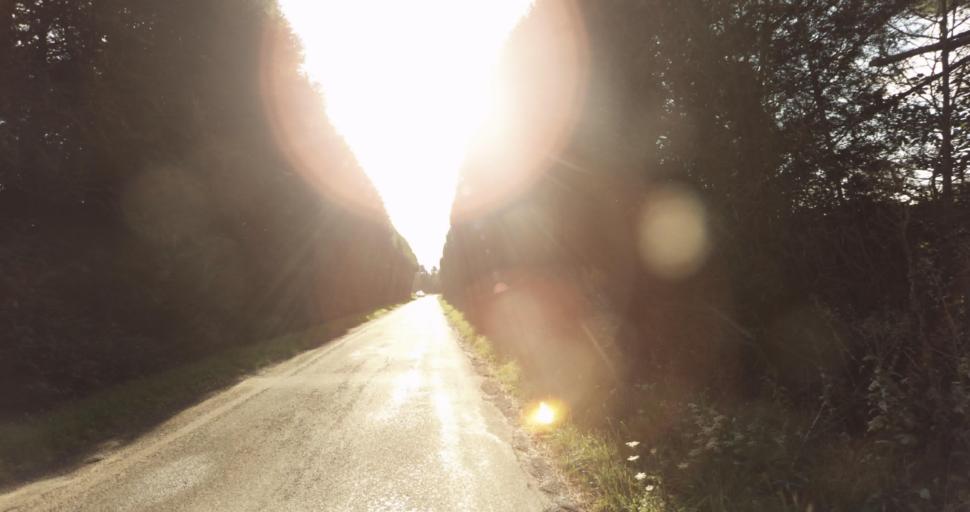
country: FR
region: Haute-Normandie
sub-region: Departement de l'Eure
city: Marcilly-sur-Eure
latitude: 48.9051
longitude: 1.3010
